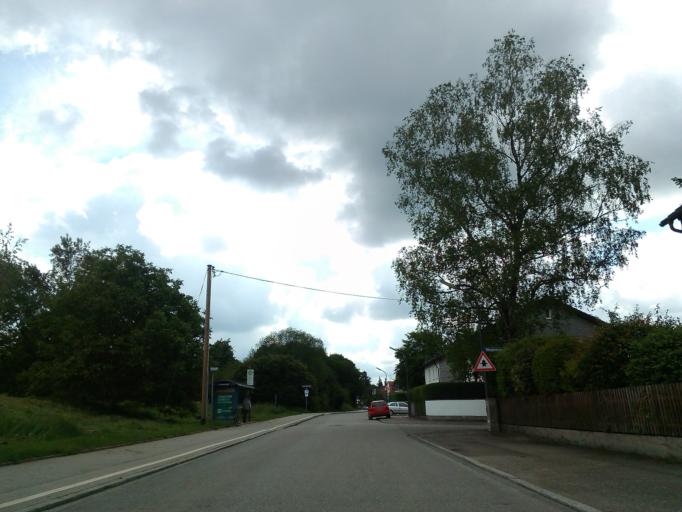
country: DE
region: Bavaria
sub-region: Upper Bavaria
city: Neubiberg
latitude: 48.1146
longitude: 11.6626
